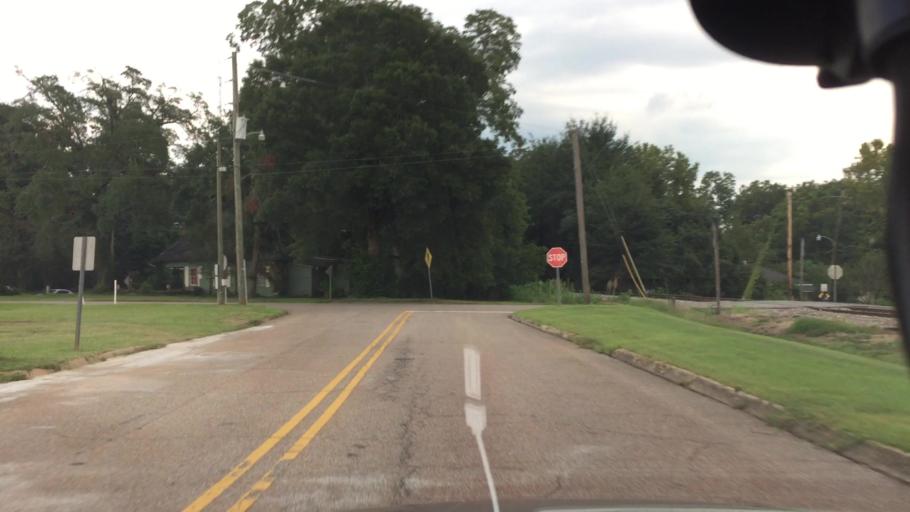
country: US
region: Alabama
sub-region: Coffee County
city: Enterprise
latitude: 31.3115
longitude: -85.8524
